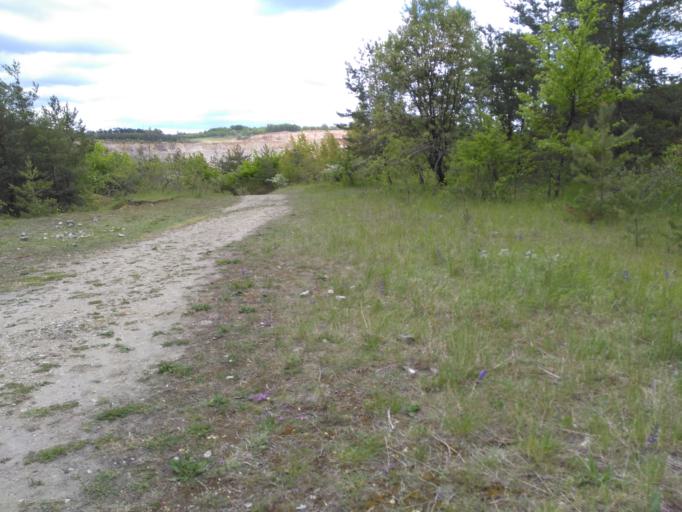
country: CZ
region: Central Bohemia
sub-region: Okres Beroun
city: Kraluv Dvur
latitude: 49.9140
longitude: 14.0671
